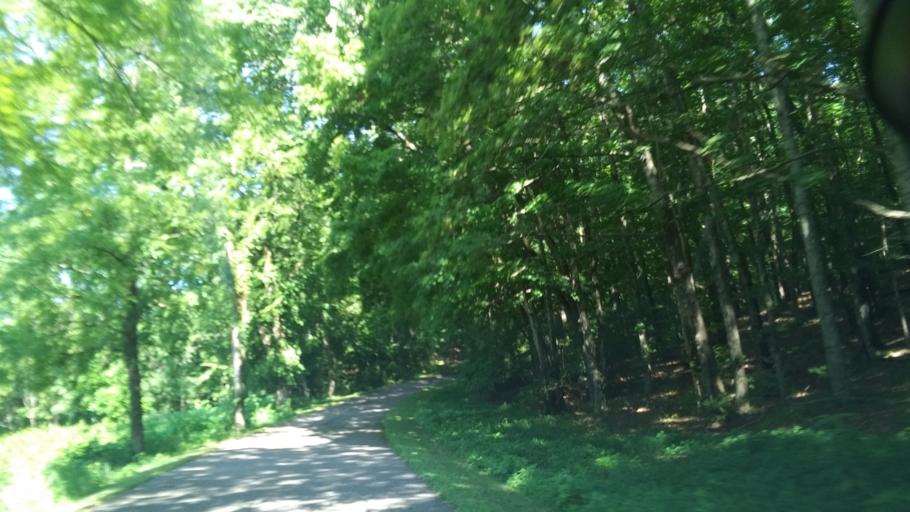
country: US
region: Tennessee
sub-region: Davidson County
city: Belle Meade
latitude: 36.0678
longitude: -86.8922
